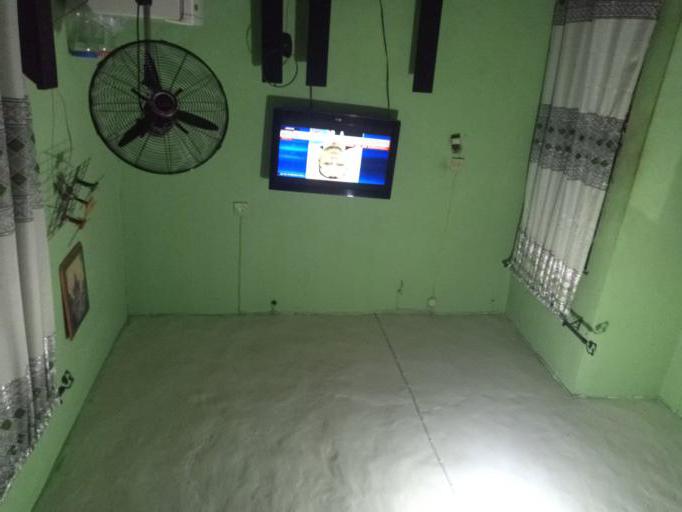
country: NG
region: Anambra
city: Onitsha
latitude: 6.1531
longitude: 6.8080
